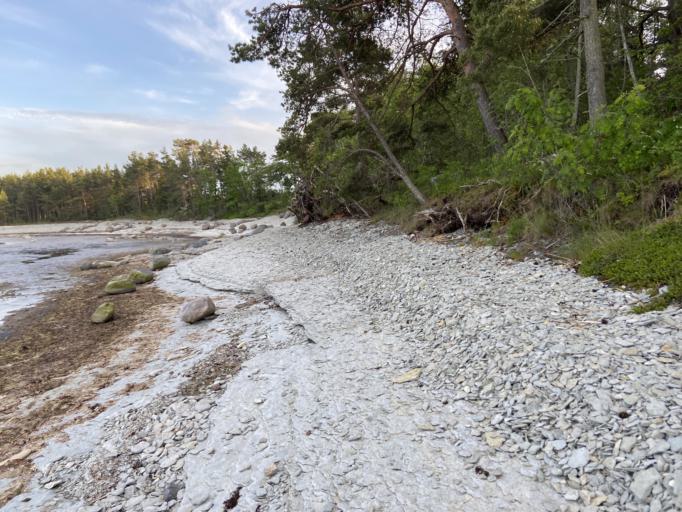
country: EE
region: Harju
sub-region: Paldiski linn
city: Paldiski
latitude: 59.2722
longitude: 23.7345
